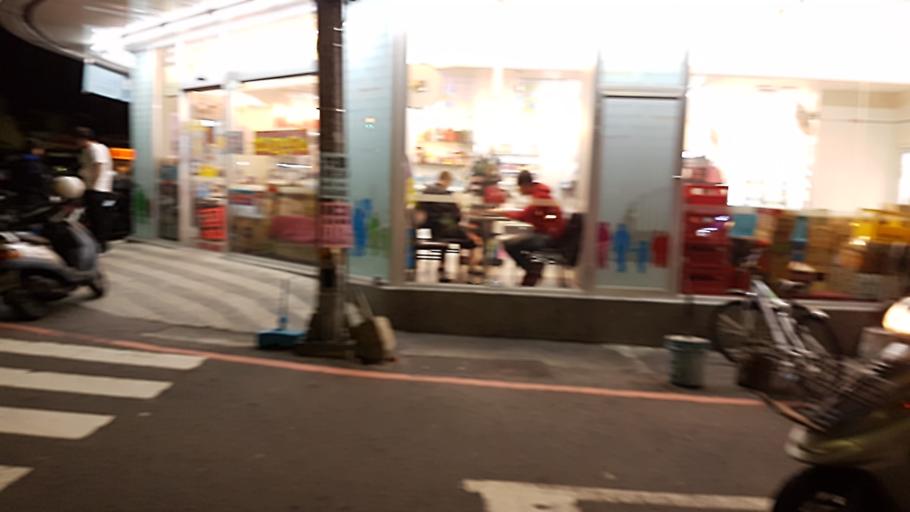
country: TW
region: Taiwan
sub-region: Hsinchu
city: Hsinchu
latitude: 24.8021
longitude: 120.9547
